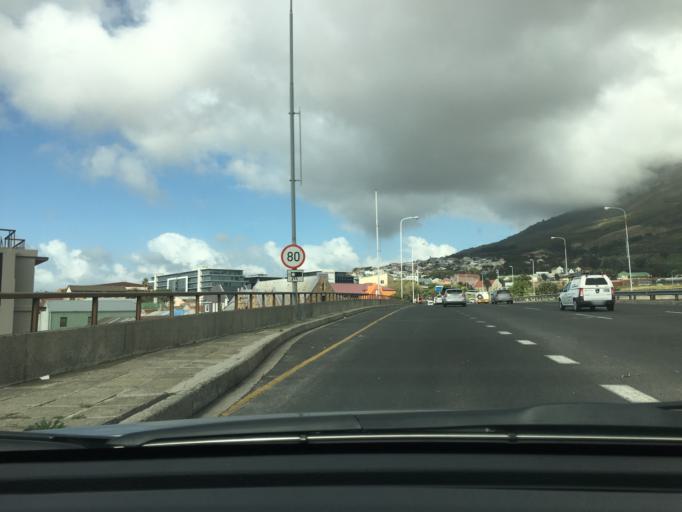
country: ZA
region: Western Cape
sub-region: City of Cape Town
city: Cape Town
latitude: -33.9284
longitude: 18.4348
